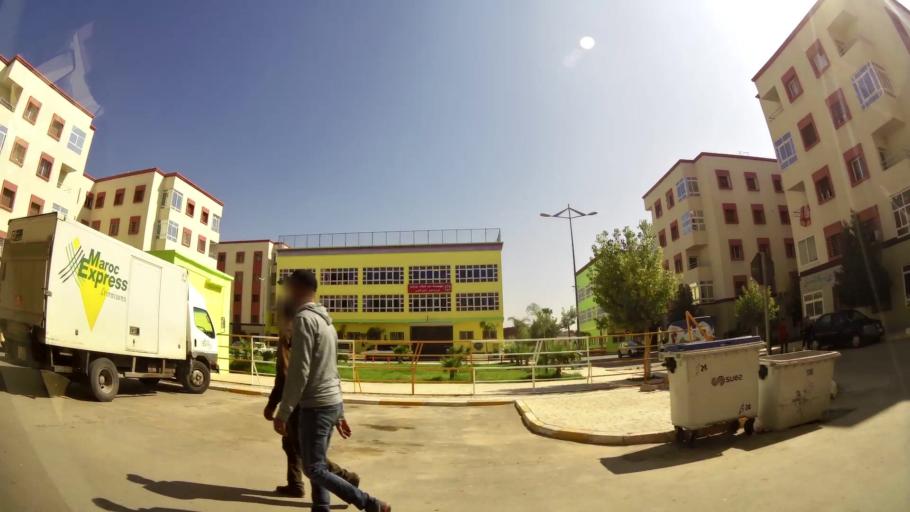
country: MA
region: Oriental
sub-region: Oujda-Angad
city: Oujda
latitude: 34.6990
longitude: -1.8743
